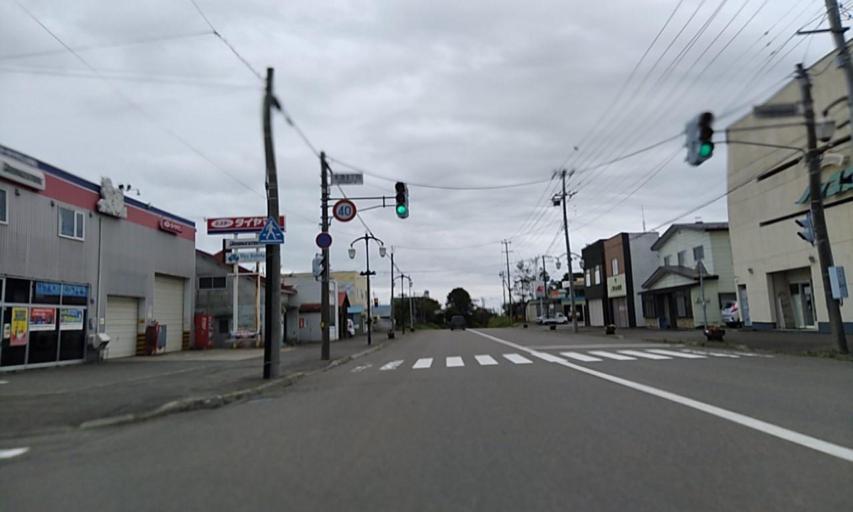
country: JP
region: Hokkaido
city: Obihiro
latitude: 42.2859
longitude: 143.3177
